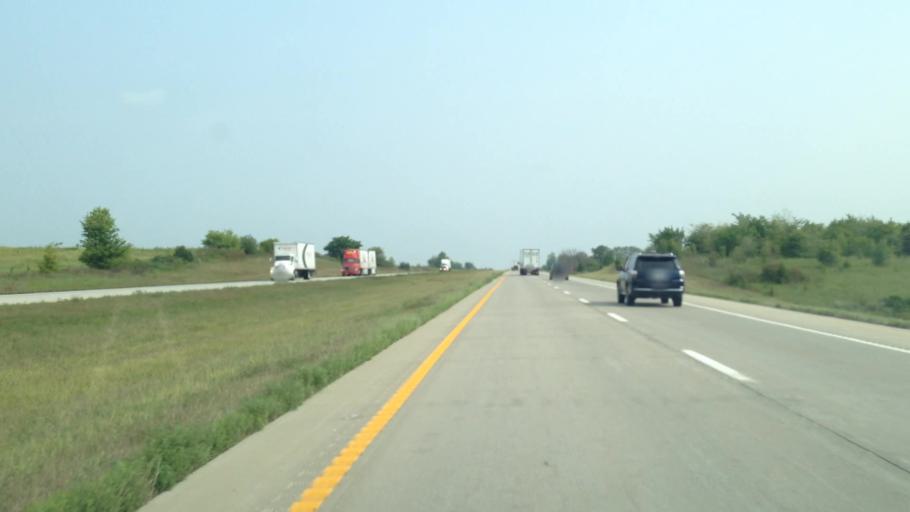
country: US
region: Missouri
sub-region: Clinton County
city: Lathrop
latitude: 39.6082
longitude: -94.2512
